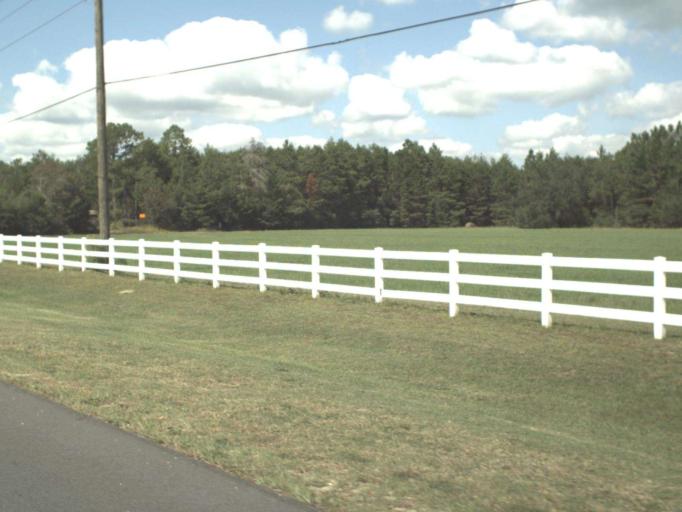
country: US
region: Florida
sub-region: Walton County
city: Freeport
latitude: 30.5082
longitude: -86.1653
